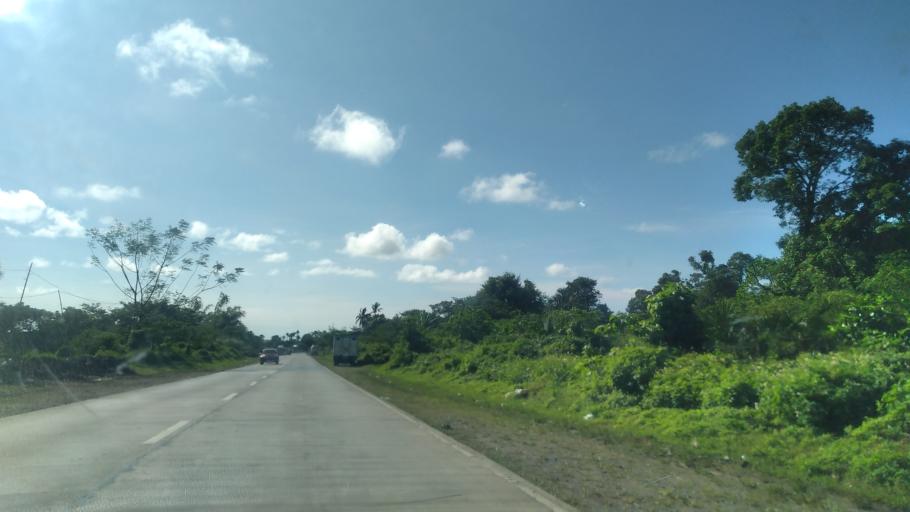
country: PH
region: Calabarzon
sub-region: Province of Quezon
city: Isabang
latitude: 13.9587
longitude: 121.5781
